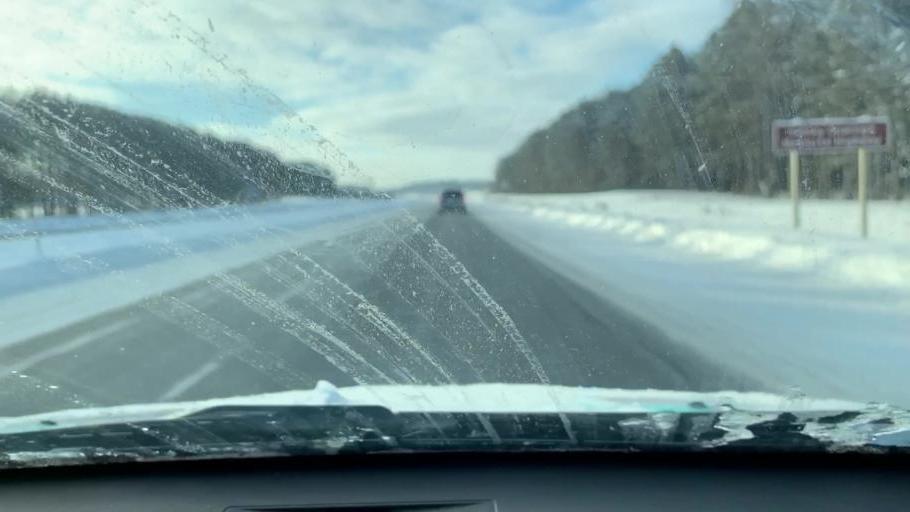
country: US
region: Michigan
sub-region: Wexford County
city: Cadillac
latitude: 44.2776
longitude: -85.3887
